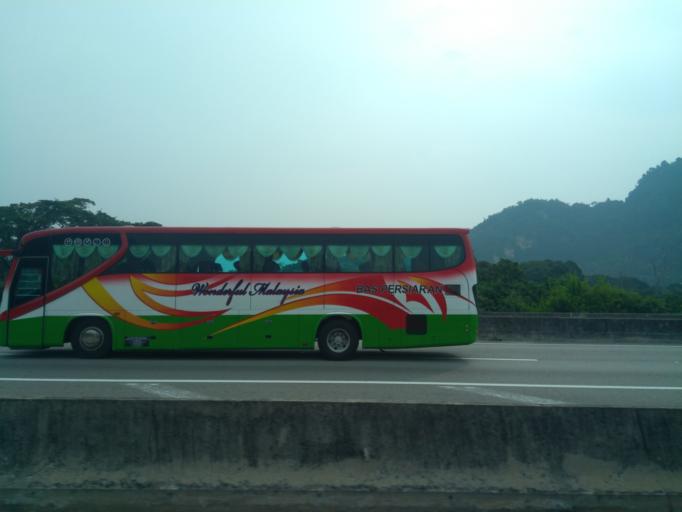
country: MY
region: Perak
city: Ipoh
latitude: 4.5940
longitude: 101.1434
